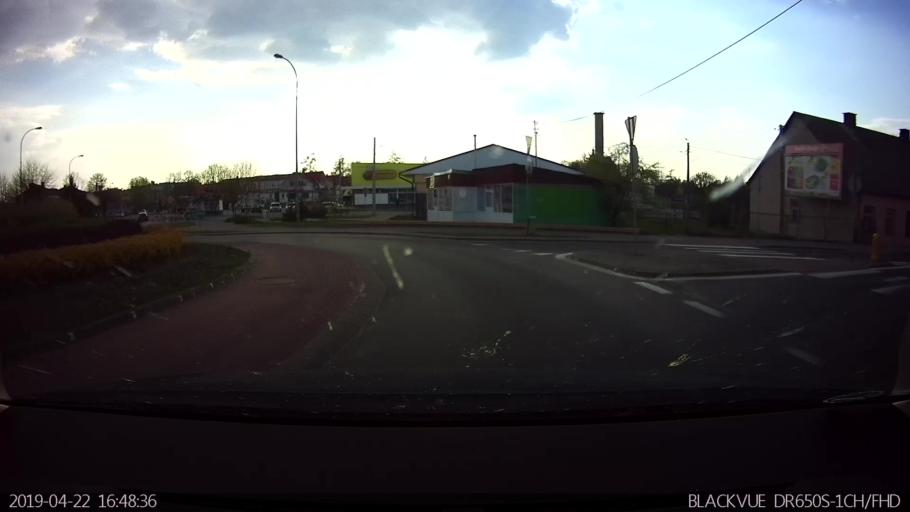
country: PL
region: Podlasie
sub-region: Powiat siemiatycki
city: Siemiatycze
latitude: 52.4284
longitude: 22.8712
